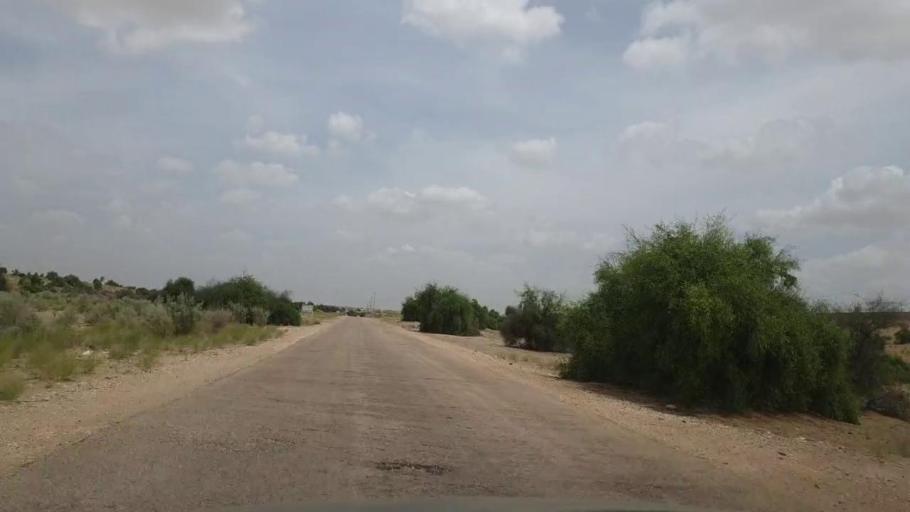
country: PK
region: Sindh
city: Kot Diji
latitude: 27.1959
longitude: 69.1598
